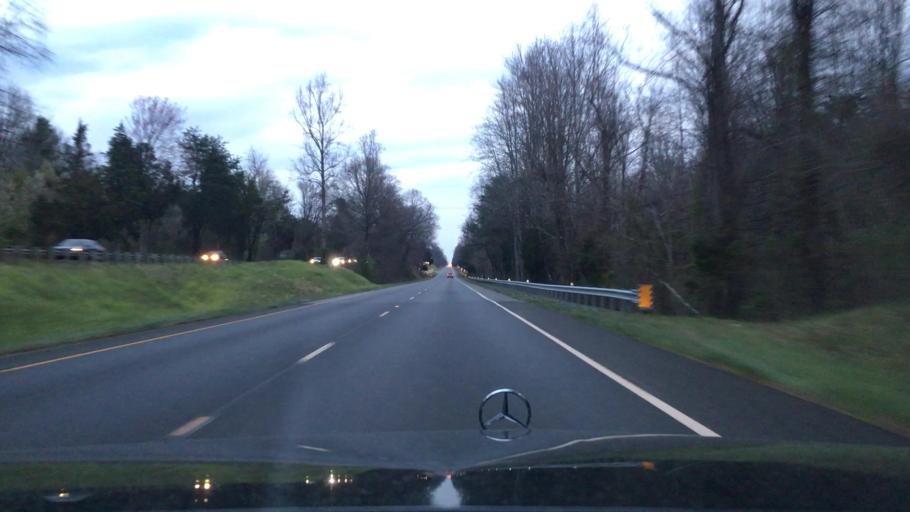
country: US
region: Virginia
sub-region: Albemarle County
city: Hollymead
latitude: 38.1663
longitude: -78.4130
